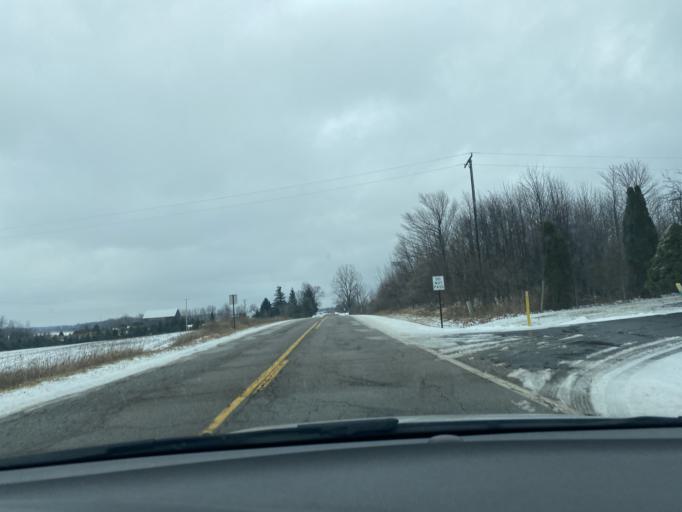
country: US
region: Michigan
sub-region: Lapeer County
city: North Branch
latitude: 43.2092
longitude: -83.1317
